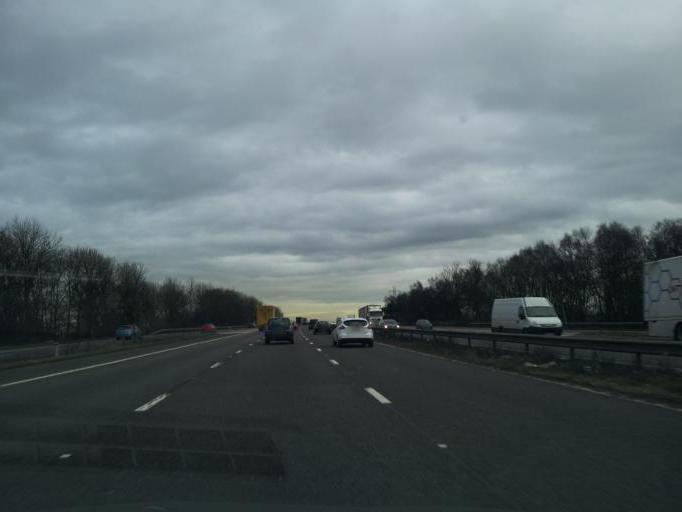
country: GB
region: England
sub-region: Warwickshire
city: Exhall
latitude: 52.4613
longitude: -1.4891
